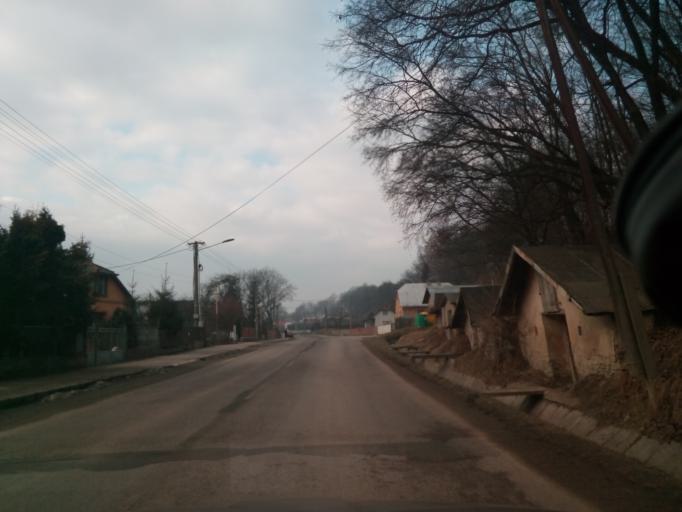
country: SK
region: Presovsky
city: Lipany
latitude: 49.1637
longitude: 20.8844
